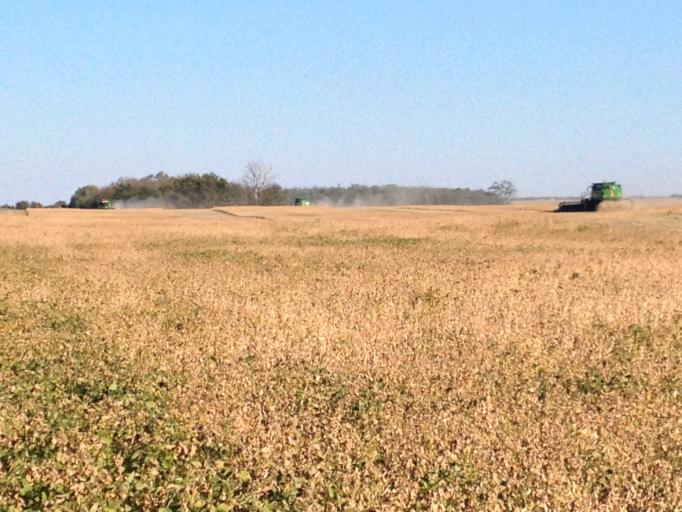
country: US
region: Kansas
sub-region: Barton County
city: Ellinwood
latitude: 38.2279
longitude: -98.6369
